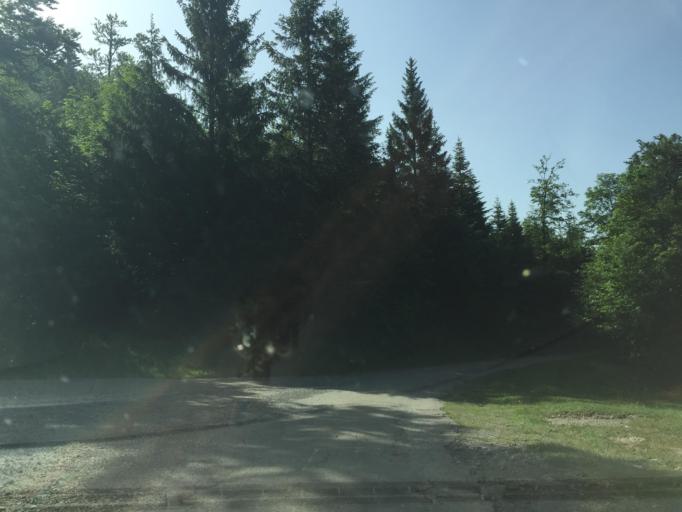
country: HR
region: Primorsko-Goranska
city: Podhum
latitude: 45.4382
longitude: 14.5624
